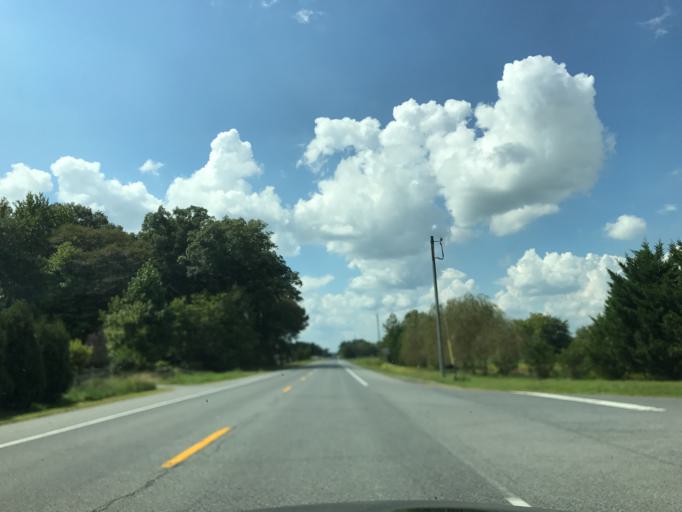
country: US
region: Delaware
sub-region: Kent County
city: Clayton
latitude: 39.1953
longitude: -75.8040
